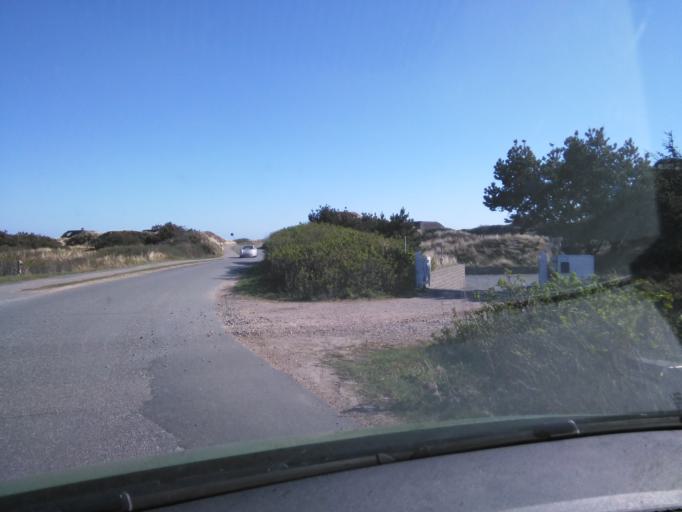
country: DK
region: South Denmark
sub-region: Varde Kommune
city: Oksbol
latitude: 55.5563
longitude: 8.0904
